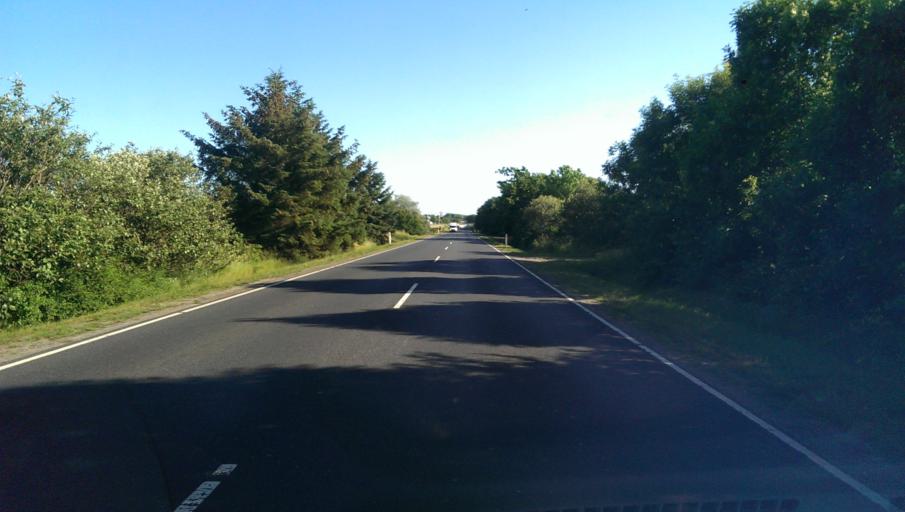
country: DK
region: South Denmark
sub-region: Esbjerg Kommune
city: Esbjerg
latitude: 55.5150
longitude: 8.4062
